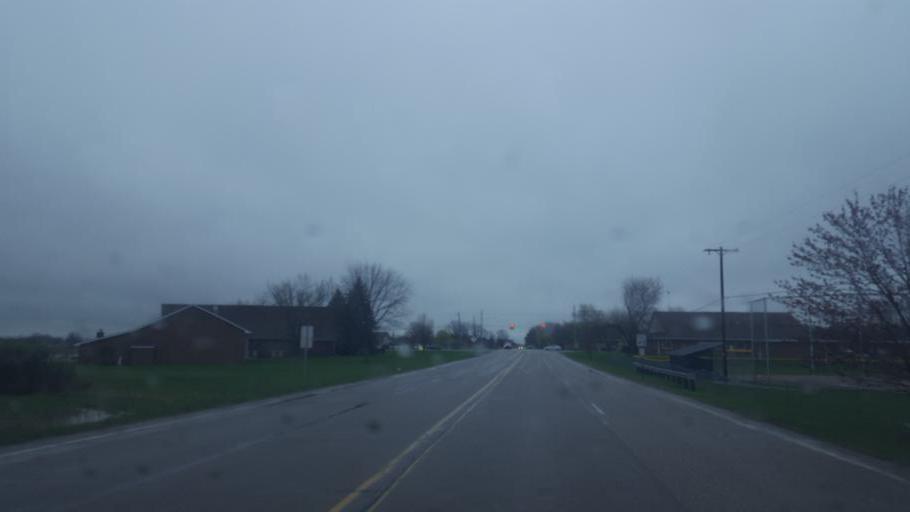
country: US
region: Michigan
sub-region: Isabella County
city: Mount Pleasant
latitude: 43.6115
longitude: -84.8102
